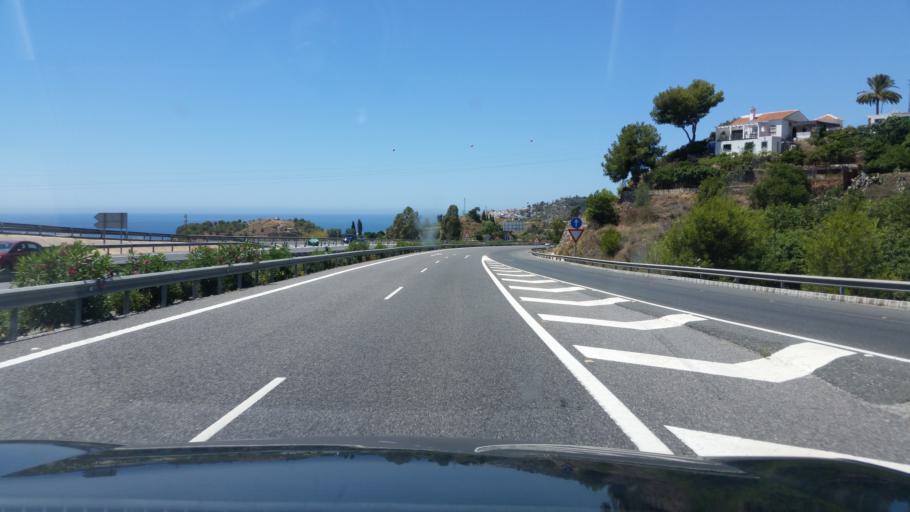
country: ES
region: Andalusia
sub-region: Provincia de Malaga
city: Nerja
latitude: 36.7612
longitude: -3.8907
